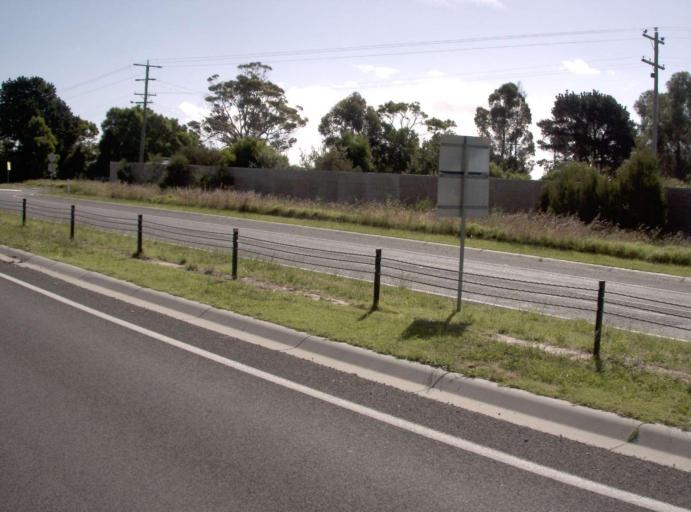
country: AU
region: Victoria
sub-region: Bass Coast
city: North Wonthaggi
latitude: -38.4157
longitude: 145.5242
